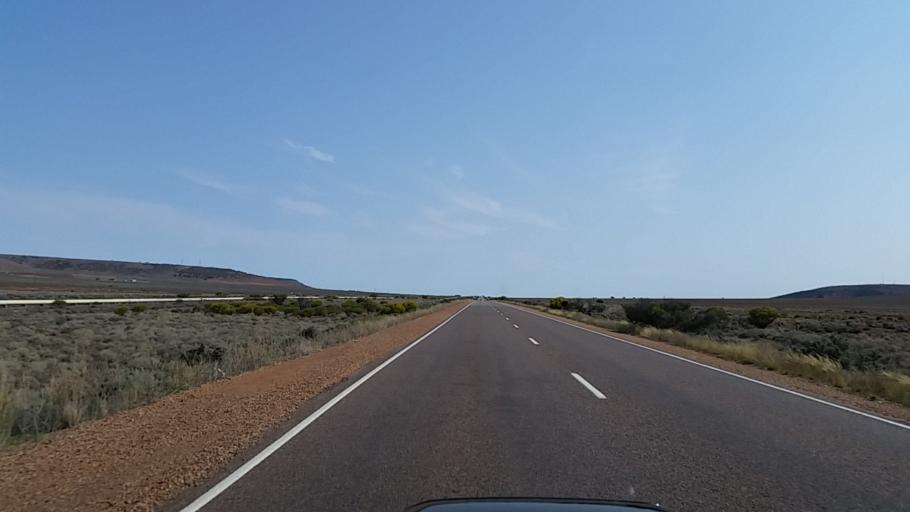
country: AU
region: South Australia
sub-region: Port Augusta
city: Port Augusta West
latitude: -32.5917
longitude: 137.6072
